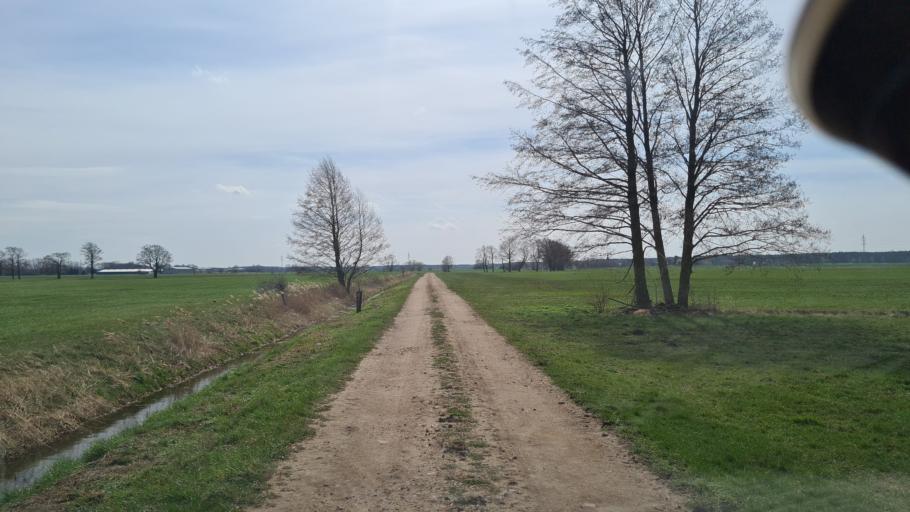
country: DE
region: Brandenburg
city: Bronkow
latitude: 51.6066
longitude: 13.9273
